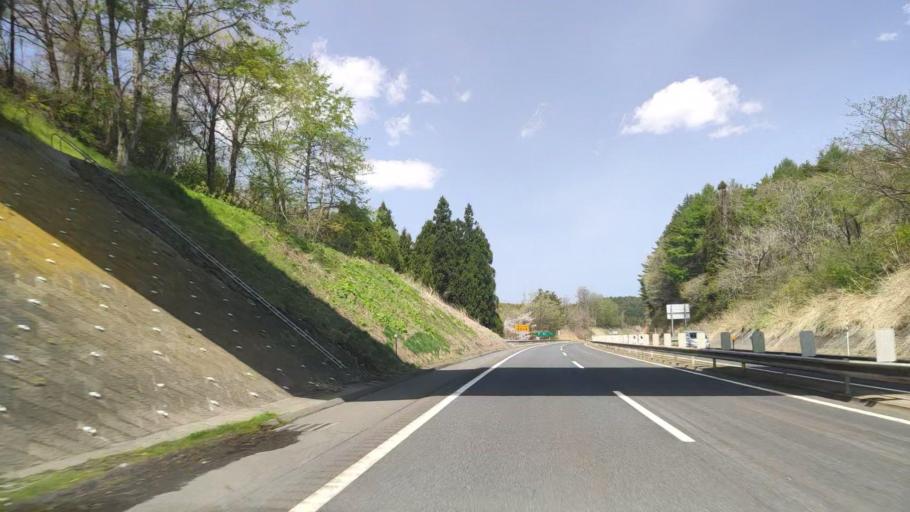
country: JP
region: Aomori
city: Hachinohe
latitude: 40.4171
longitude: 141.4410
